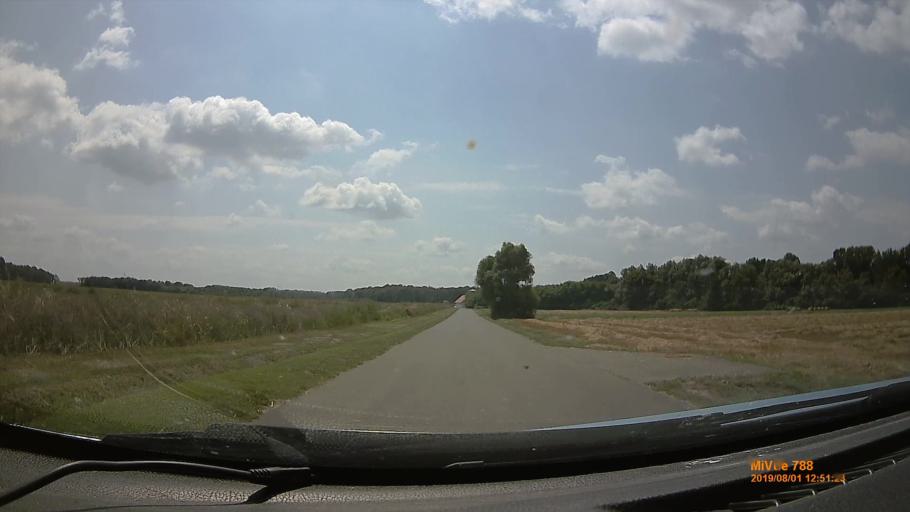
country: HR
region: Osjecko-Baranjska
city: Viljevo
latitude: 45.8037
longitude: 18.1007
